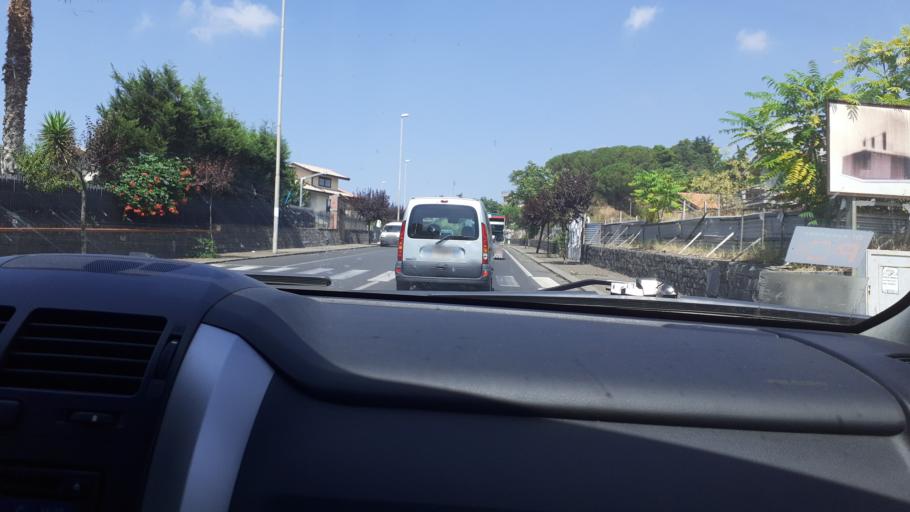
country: IT
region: Sicily
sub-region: Catania
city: Nicolosi
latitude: 37.6157
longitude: 15.0343
